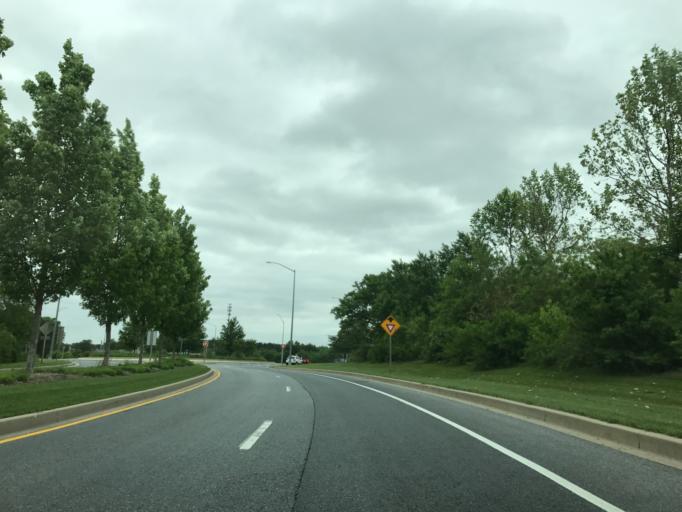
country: US
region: Maryland
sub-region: Carroll County
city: Hampstead
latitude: 39.5811
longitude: -76.8414
